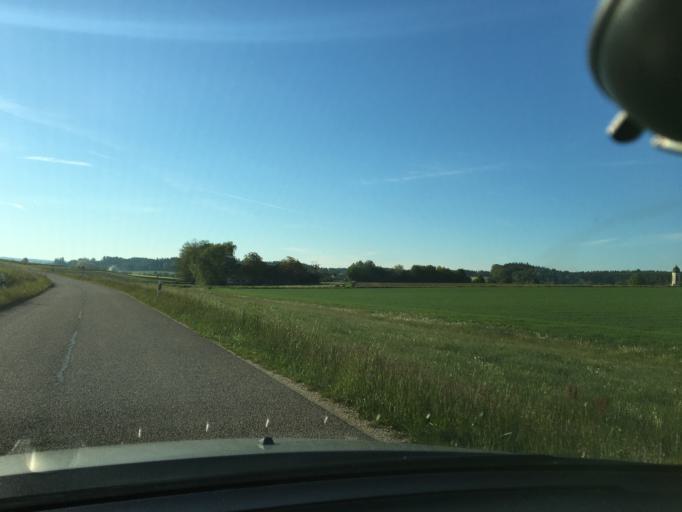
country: DE
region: Bavaria
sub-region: Lower Bavaria
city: Vilsbiburg
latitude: 48.5030
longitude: 12.3422
